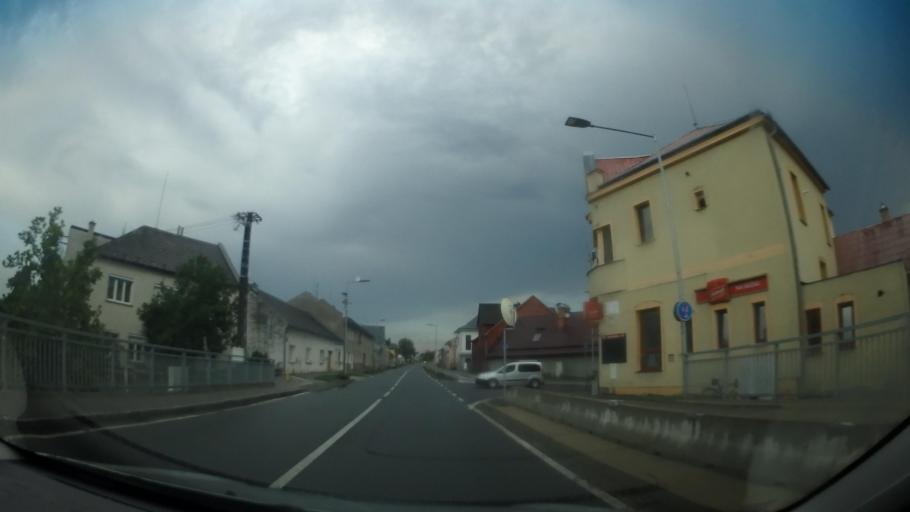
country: CZ
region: Olomoucky
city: Lostice
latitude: 49.7442
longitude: 16.9322
